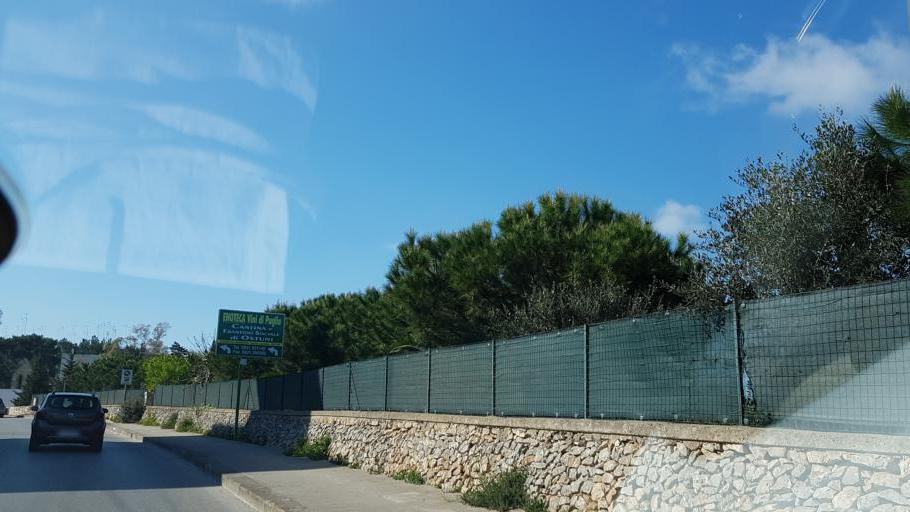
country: IT
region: Apulia
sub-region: Provincia di Brindisi
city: Ostuni
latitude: 40.7250
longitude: 17.5873
